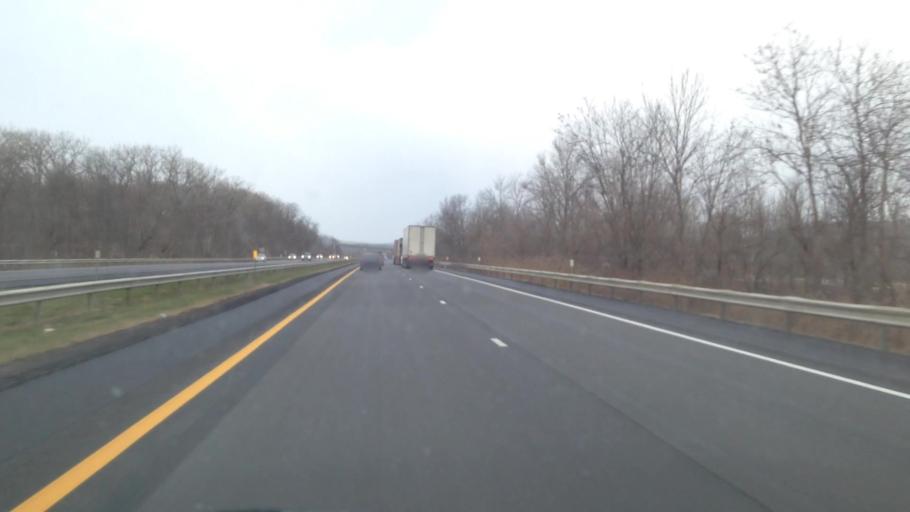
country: US
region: New York
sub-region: Montgomery County
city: Fonda
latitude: 42.9383
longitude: -74.3346
